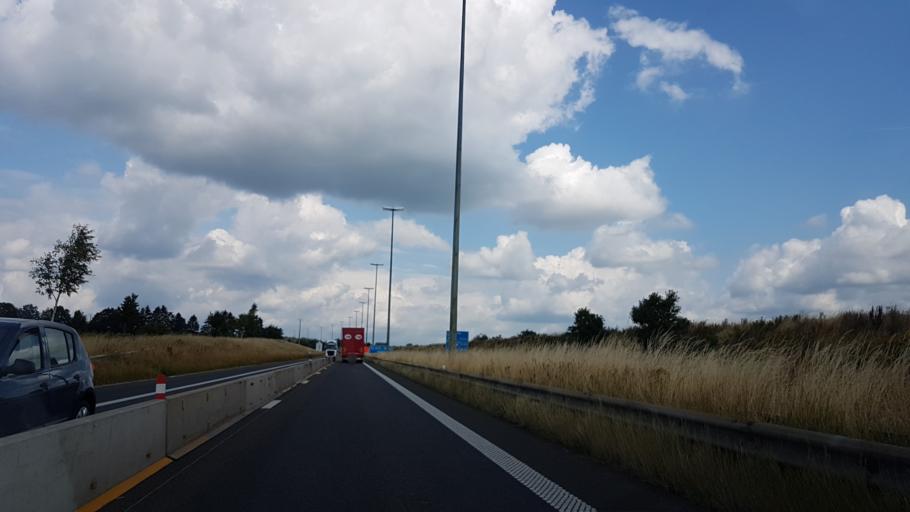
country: BE
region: Wallonia
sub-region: Province de Liege
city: Saint-Vith
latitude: 50.2775
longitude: 6.1092
